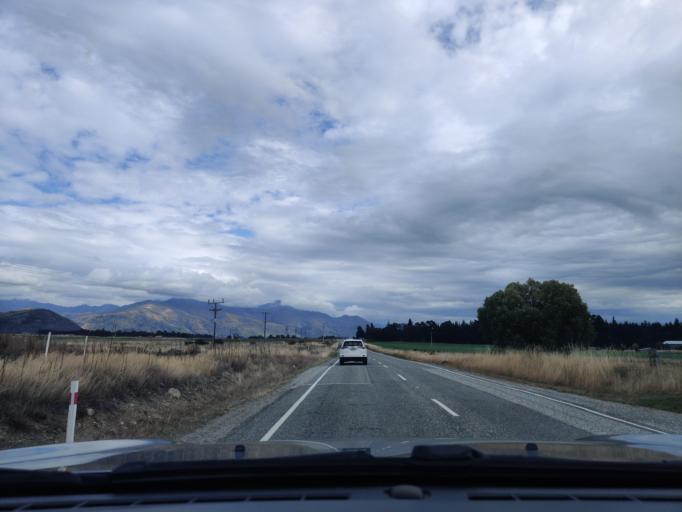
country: NZ
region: Otago
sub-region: Queenstown-Lakes District
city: Wanaka
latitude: -44.7225
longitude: 169.2367
